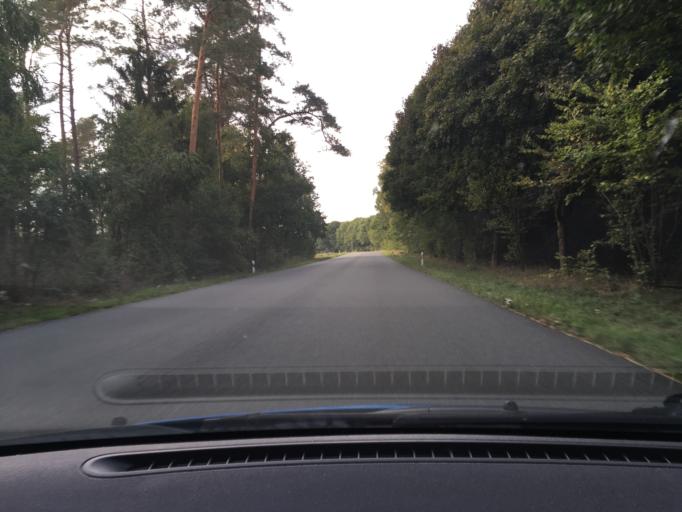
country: DE
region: Lower Saxony
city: Munster
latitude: 52.9159
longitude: 10.0786
